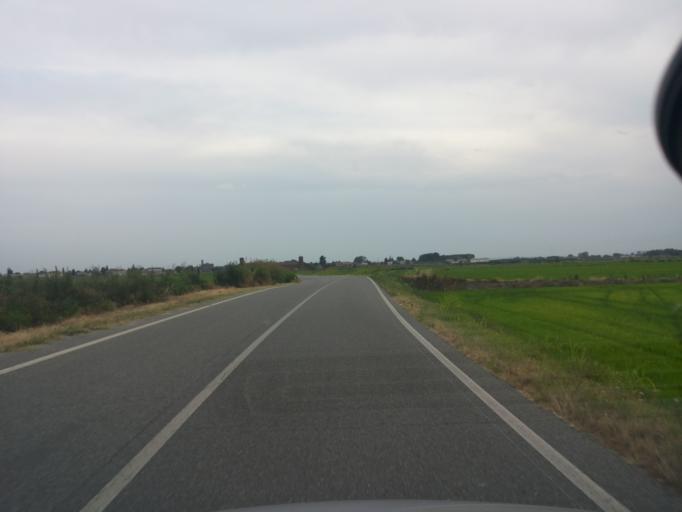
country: IT
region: Piedmont
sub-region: Provincia di Vercelli
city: Prarolo
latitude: 45.2749
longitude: 8.4829
